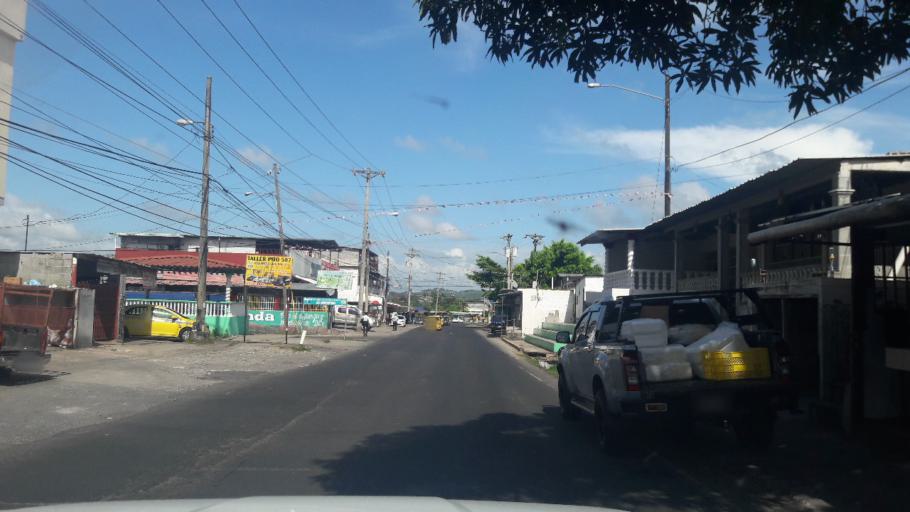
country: PA
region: Panama
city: San Miguelito
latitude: 9.0735
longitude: -79.4902
